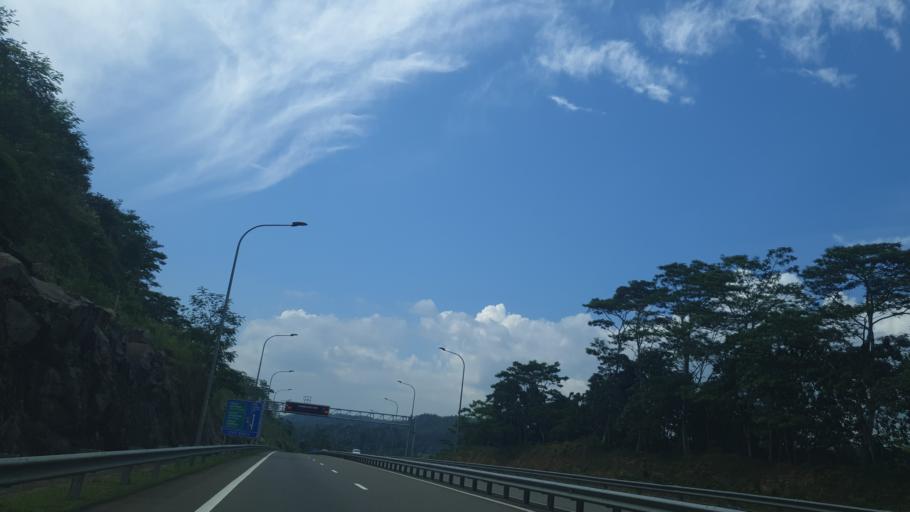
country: LK
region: Southern
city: Weligama
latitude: 6.0338
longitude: 80.3704
